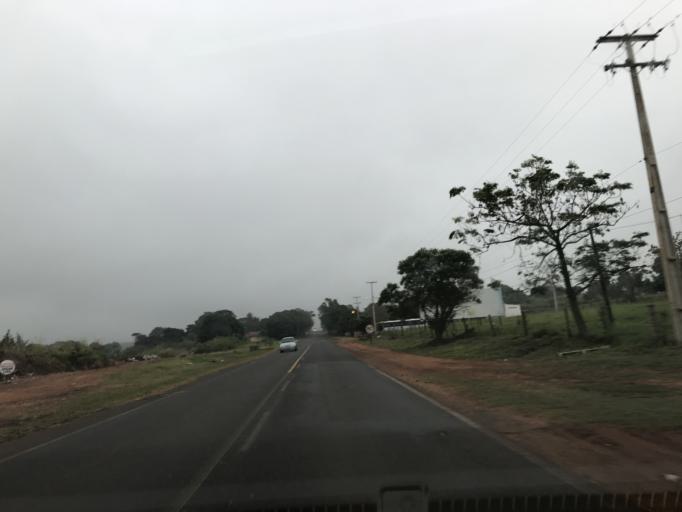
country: PY
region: Canindeyu
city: Salto del Guaira
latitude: -24.1523
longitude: -54.1026
